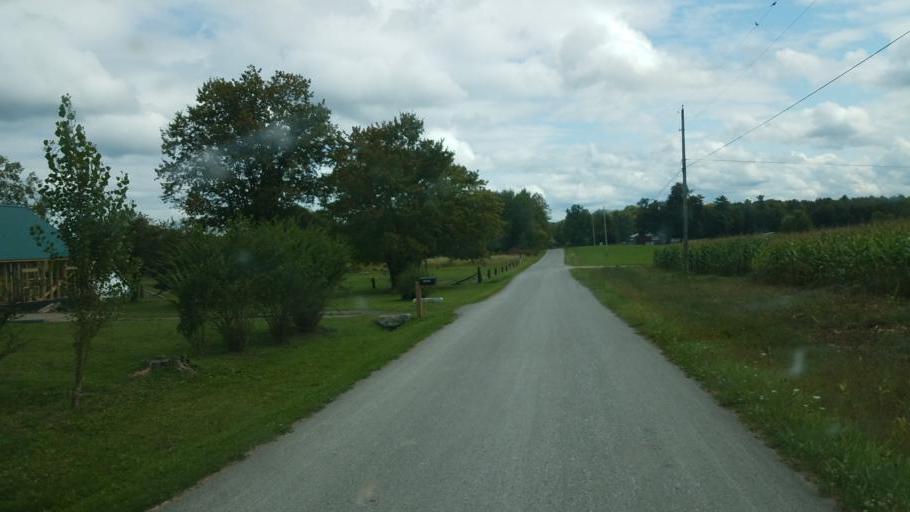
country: US
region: Pennsylvania
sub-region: Crawford County
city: Conneaut Lakeshore
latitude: 41.4829
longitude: -80.2391
